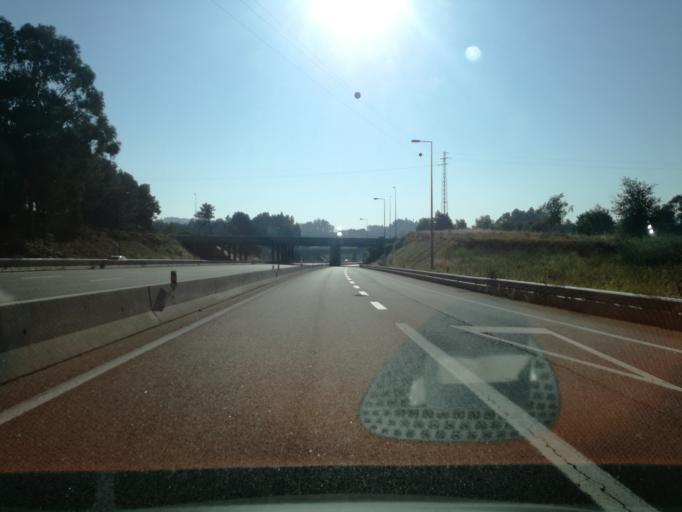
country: PT
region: Porto
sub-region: Maia
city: Nogueira
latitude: 41.2407
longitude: -8.5664
